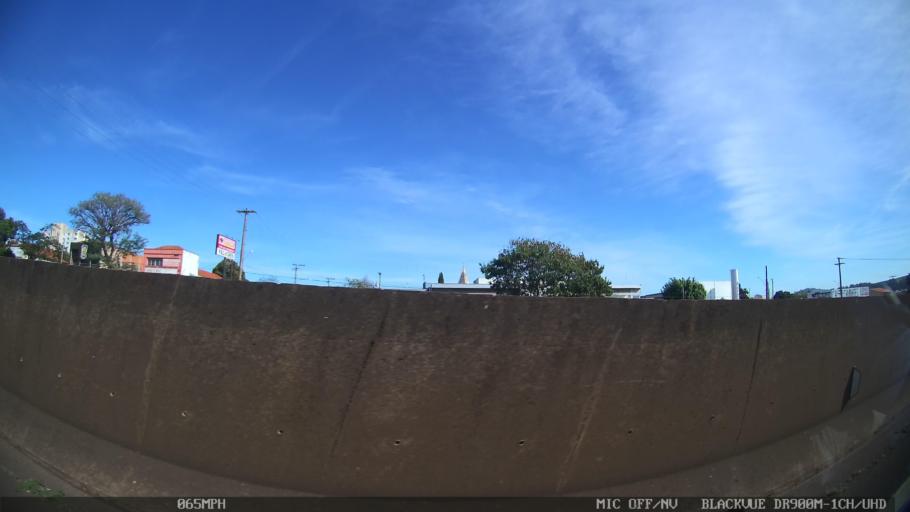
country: BR
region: Sao Paulo
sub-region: Araras
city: Araras
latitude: -22.3525
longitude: -47.3947
